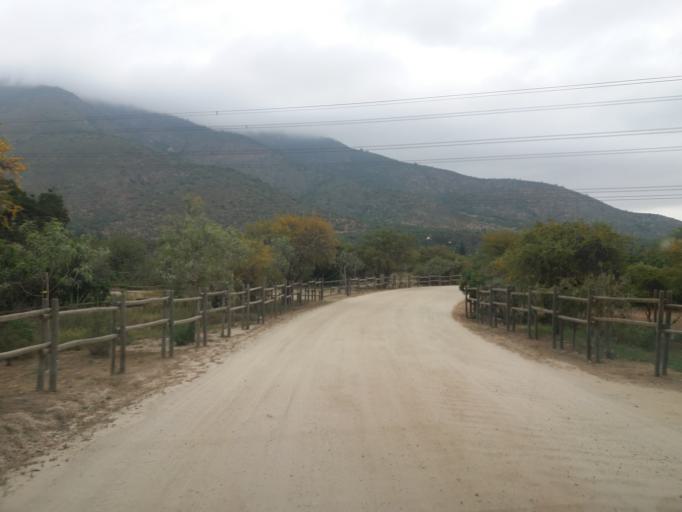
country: CL
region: Valparaiso
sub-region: Provincia de Marga Marga
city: Limache
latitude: -33.0273
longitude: -71.1397
